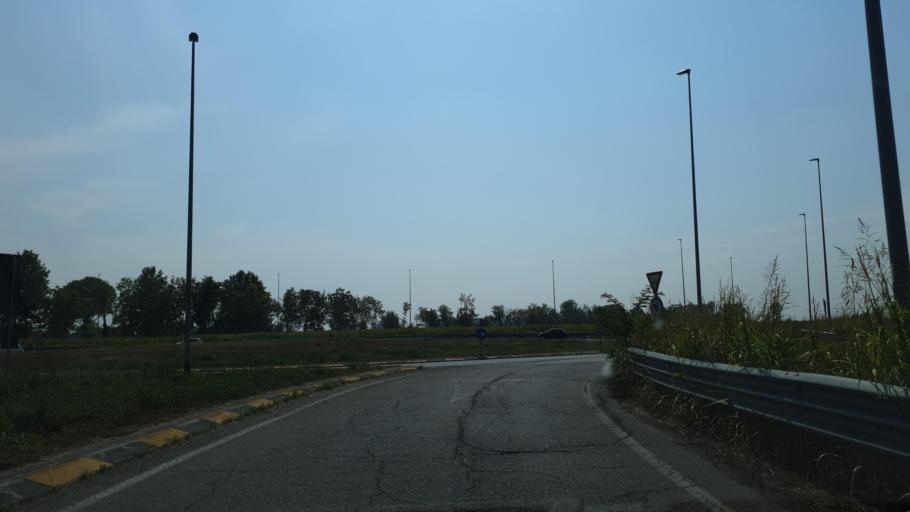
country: IT
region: Lombardy
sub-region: Provincia di Brescia
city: Ghedi
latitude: 45.3871
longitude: 10.2498
